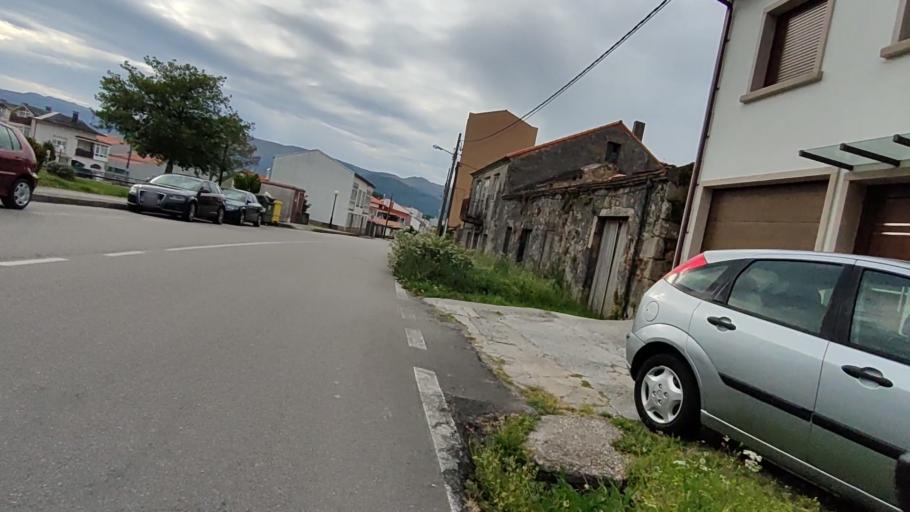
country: ES
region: Galicia
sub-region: Provincia da Coruna
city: Boiro
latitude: 42.6355
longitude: -8.8737
